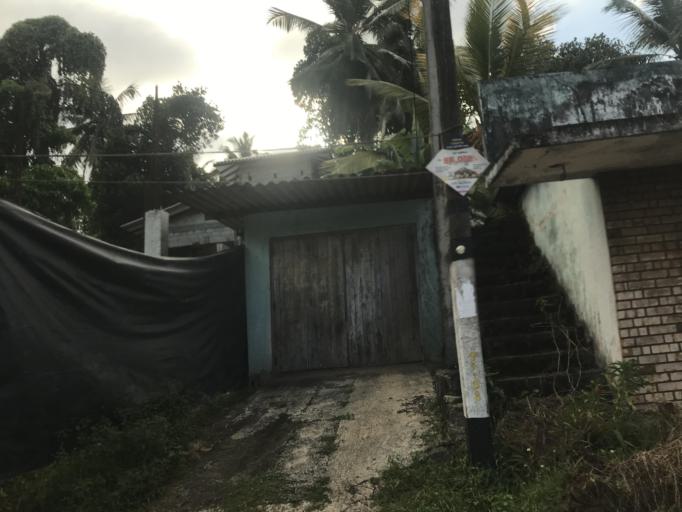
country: LK
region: Western
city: Gampaha
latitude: 7.0772
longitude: 79.9907
